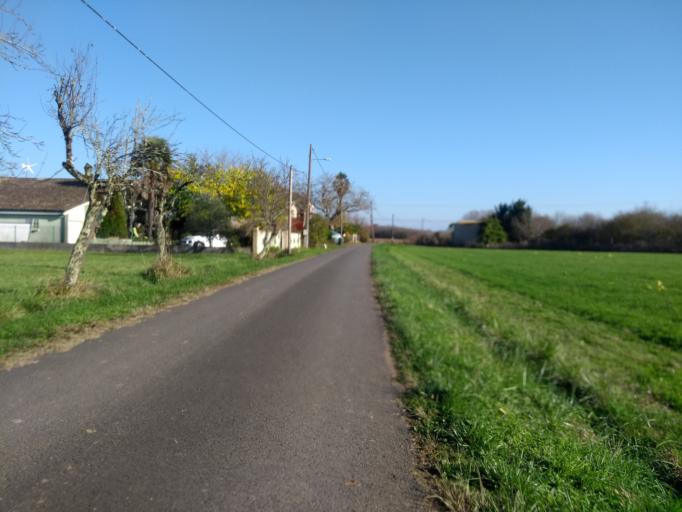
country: FR
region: Aquitaine
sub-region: Departement de la Gironde
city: Cambes
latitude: 44.7312
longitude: -0.4828
